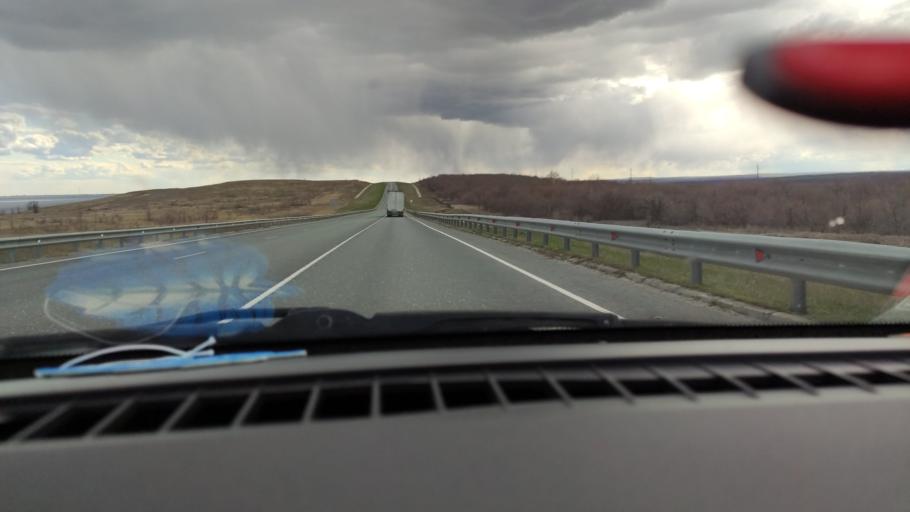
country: RU
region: Saratov
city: Alekseyevka
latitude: 52.2101
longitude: 47.8805
